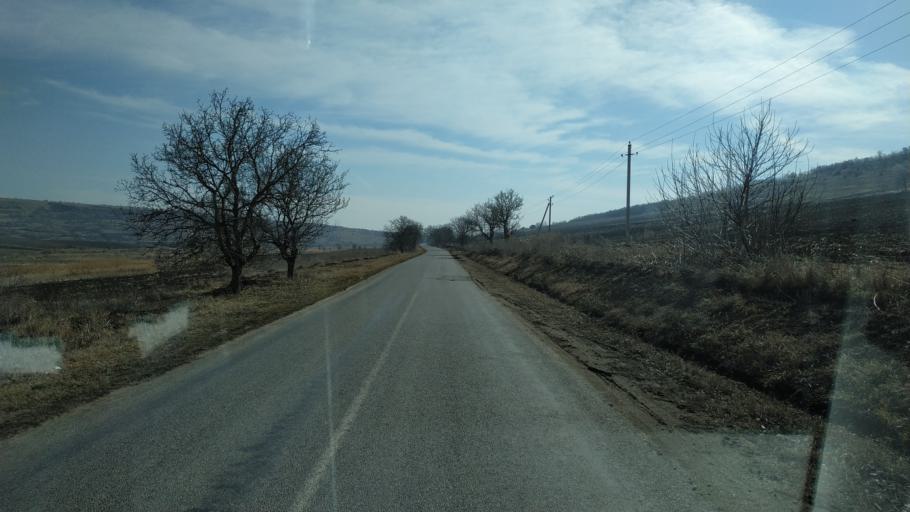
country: MD
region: Nisporeni
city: Nisporeni
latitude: 47.1388
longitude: 28.1156
